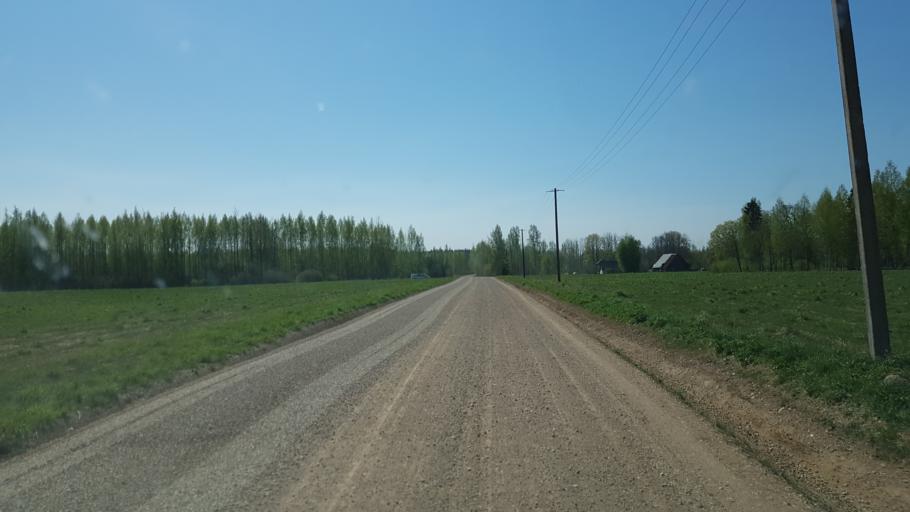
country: EE
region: Polvamaa
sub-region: Polva linn
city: Polva
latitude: 58.1182
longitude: 27.2379
